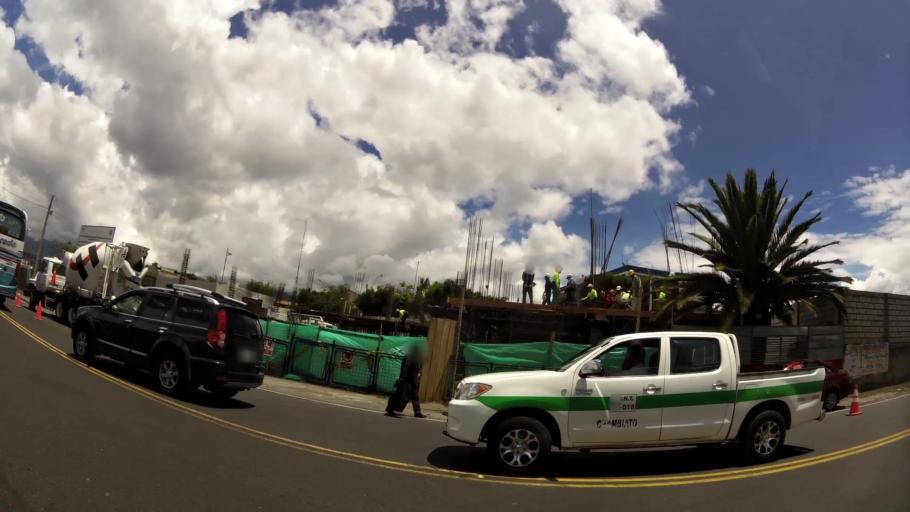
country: EC
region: Tungurahua
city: Pelileo
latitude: -1.3277
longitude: -78.5491
